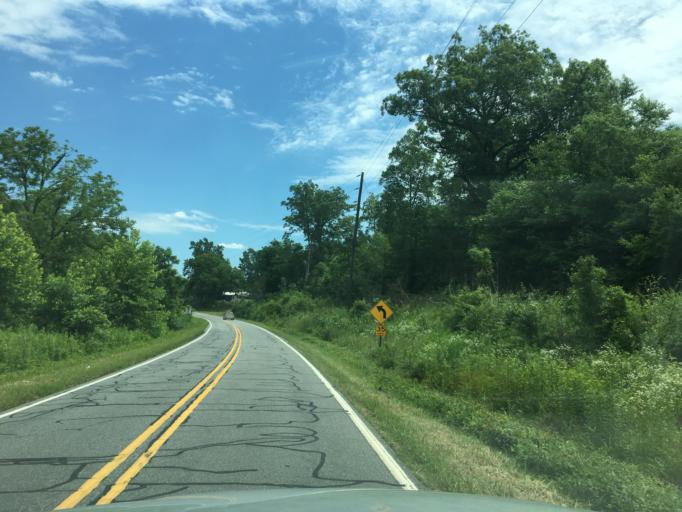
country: US
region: North Carolina
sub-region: Rutherford County
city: Rutherfordton
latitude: 35.3081
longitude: -82.0004
